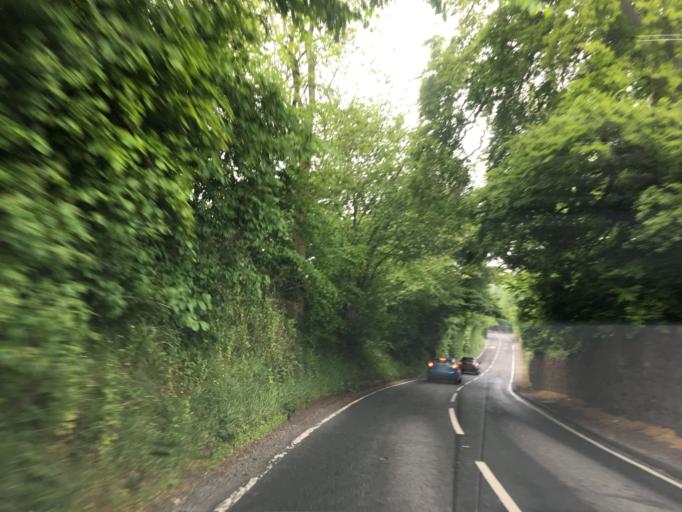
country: GB
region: Scotland
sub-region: Midlothian
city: Penicuik
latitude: 55.8398
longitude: -3.1991
